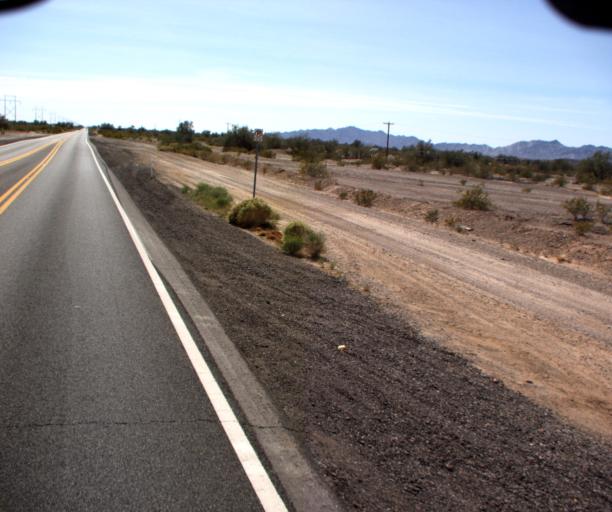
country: US
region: Arizona
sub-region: La Paz County
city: Quartzsite
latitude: 33.6509
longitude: -114.2171
